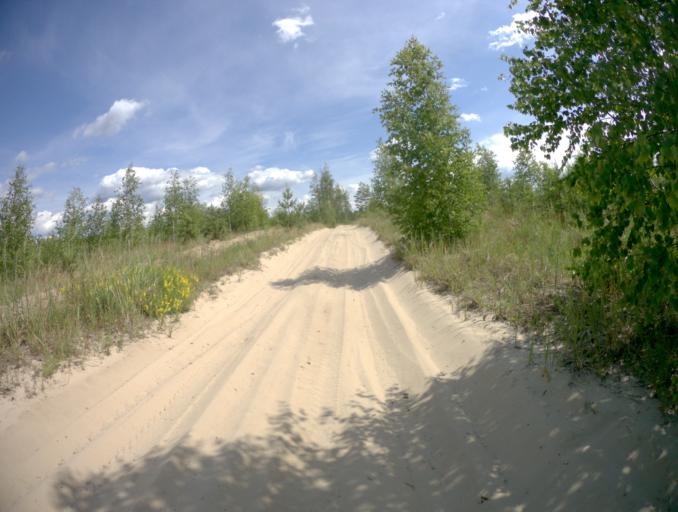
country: RU
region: Nizjnij Novgorod
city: Frolishchi
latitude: 56.4784
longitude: 42.5924
